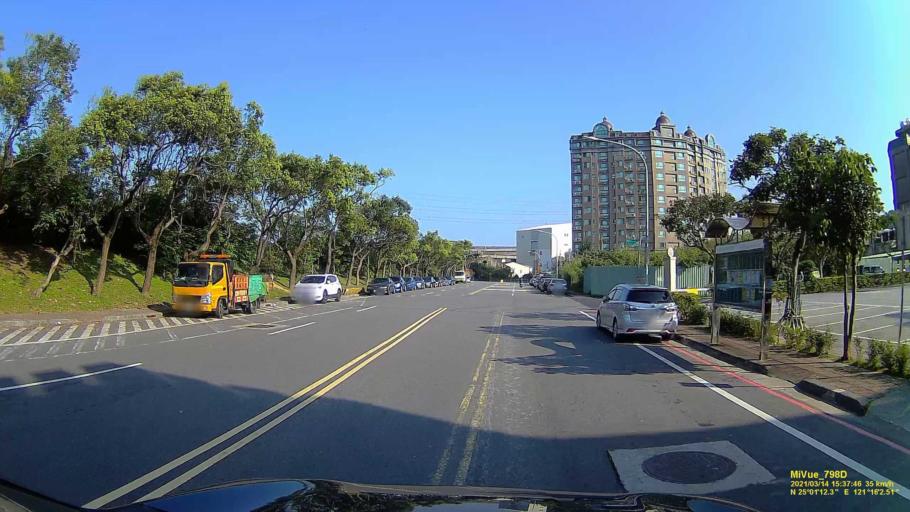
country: TW
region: Taiwan
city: Taoyuan City
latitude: 25.0200
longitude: 121.2675
